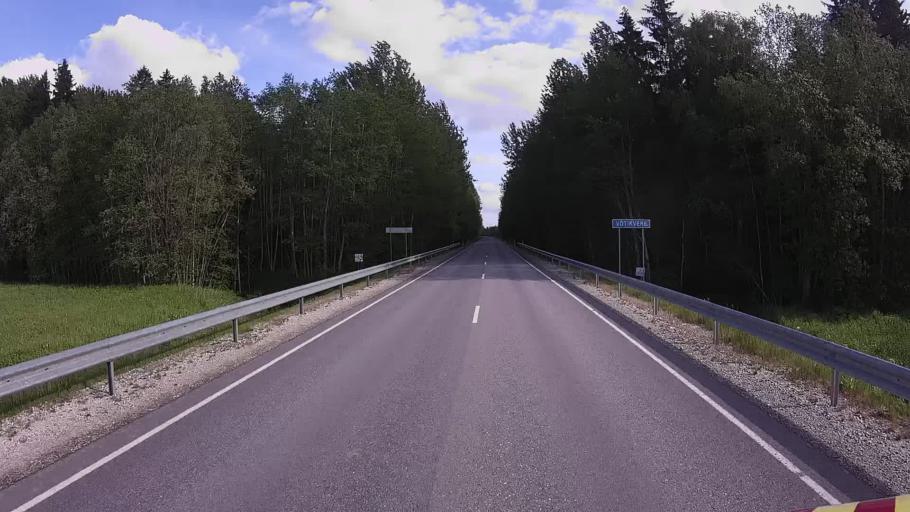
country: EE
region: Jogevamaa
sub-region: Mustvee linn
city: Mustvee
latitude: 58.8856
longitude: 26.8136
